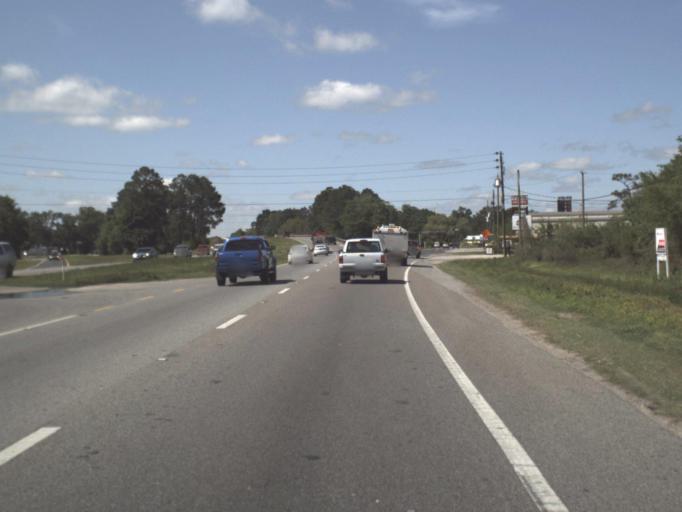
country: US
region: Florida
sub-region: Escambia County
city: Ensley
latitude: 30.5297
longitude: -87.2755
